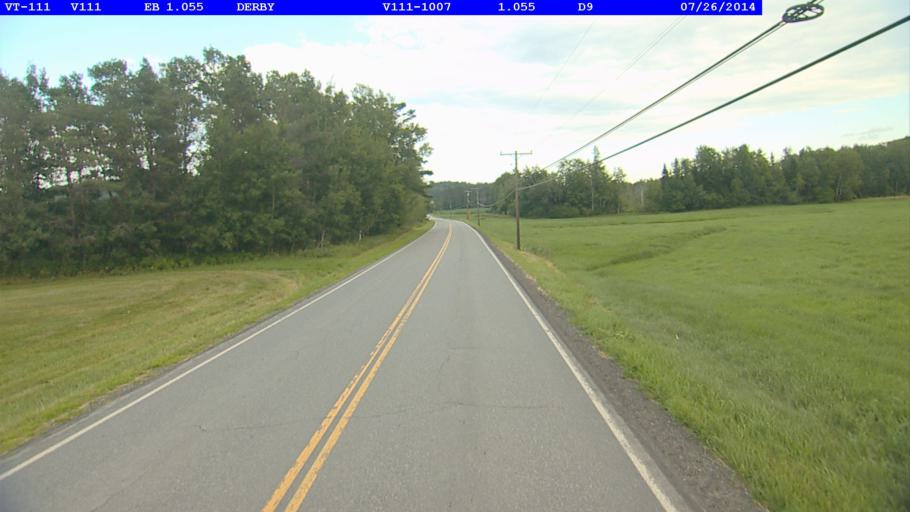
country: US
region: Vermont
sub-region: Orleans County
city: Newport
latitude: 44.9474
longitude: -72.1128
